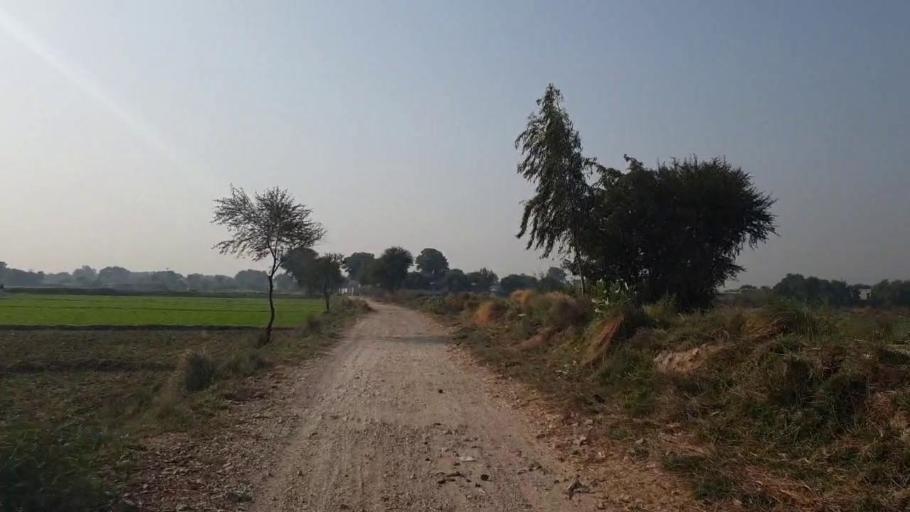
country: PK
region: Sindh
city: Kotri
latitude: 25.3393
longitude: 68.3214
